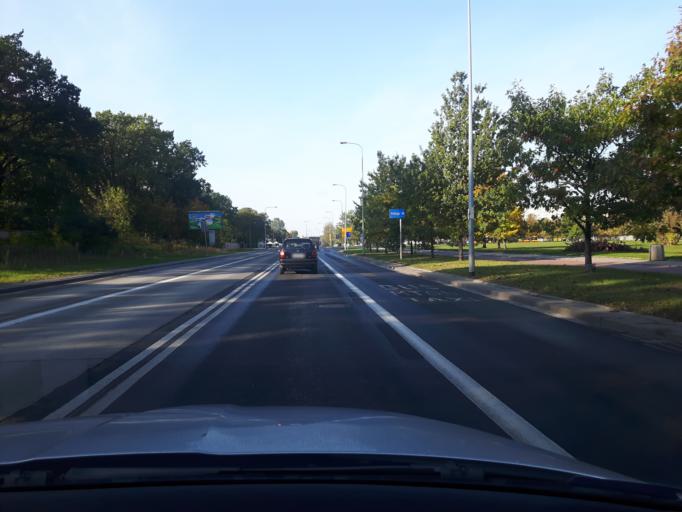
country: PL
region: Masovian Voivodeship
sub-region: Warszawa
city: Targowek
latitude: 52.2857
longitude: 21.0441
